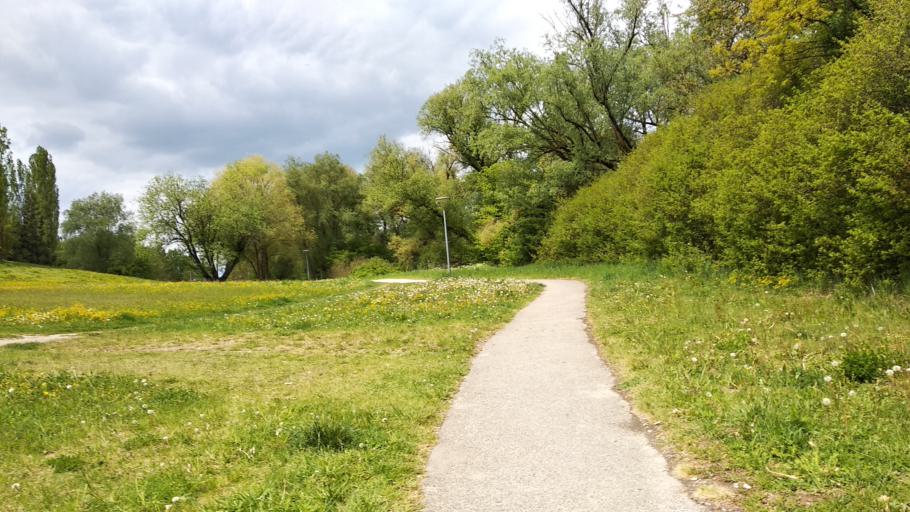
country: DE
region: Bavaria
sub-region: Upper Bavaria
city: Freising
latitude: 48.4007
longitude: 11.7222
